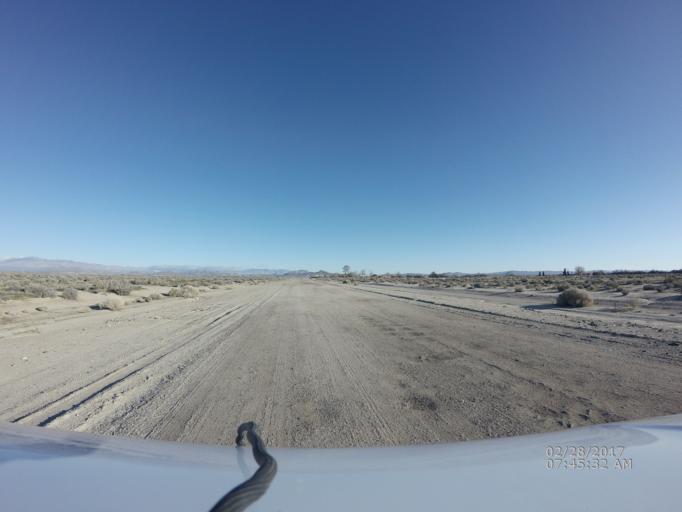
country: US
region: California
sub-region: Kern County
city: Rosamond
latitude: 34.8015
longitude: -118.1853
